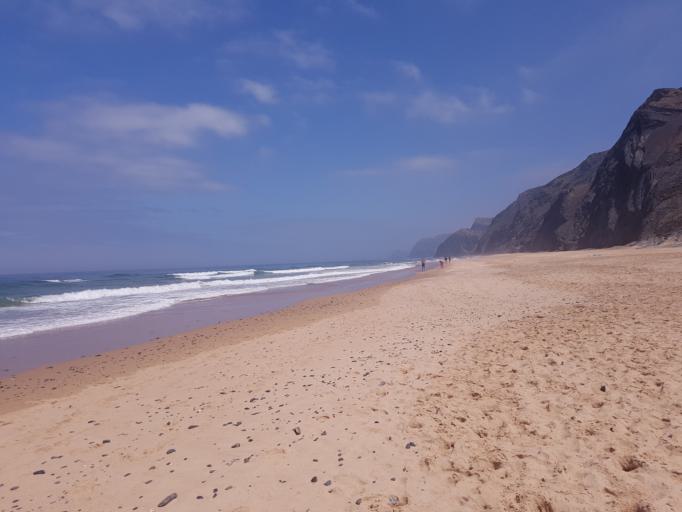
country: PT
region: Faro
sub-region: Vila do Bispo
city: Vila do Bispo
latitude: 37.1105
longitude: -8.9367
